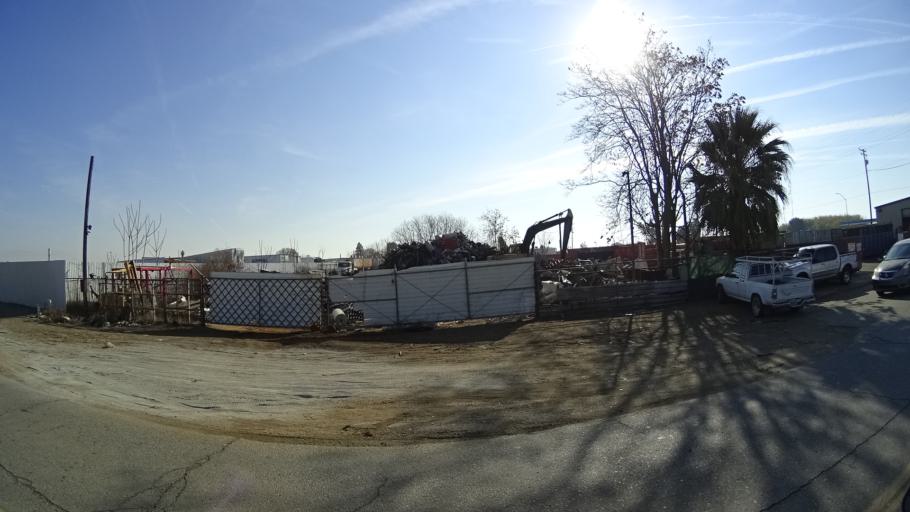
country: US
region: California
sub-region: Kern County
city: Bakersfield
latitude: 35.3249
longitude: -119.0021
